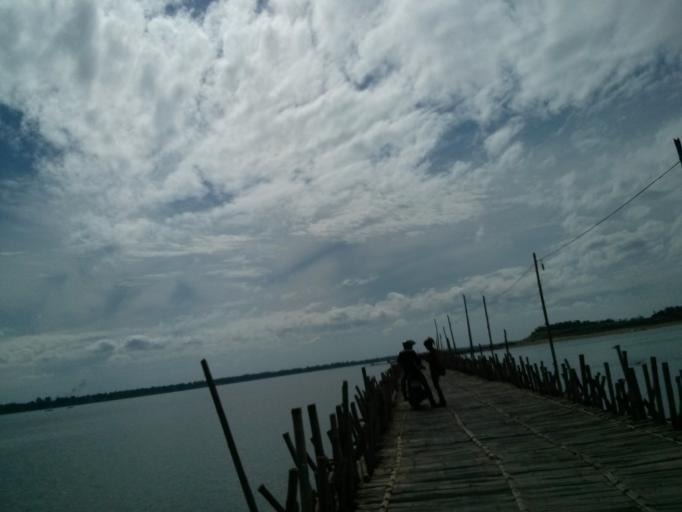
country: KH
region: Kampong Cham
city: Kampong Cham
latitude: 11.9770
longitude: 105.4615
